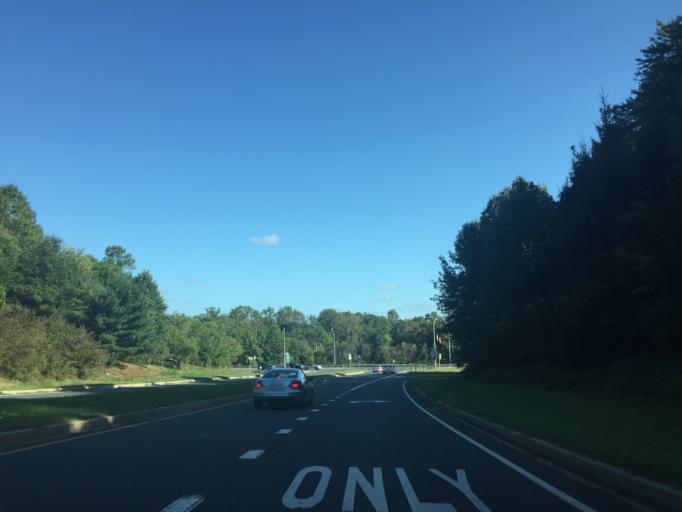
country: US
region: Maryland
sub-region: Baltimore County
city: Overlea
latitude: 39.3813
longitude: -76.4958
